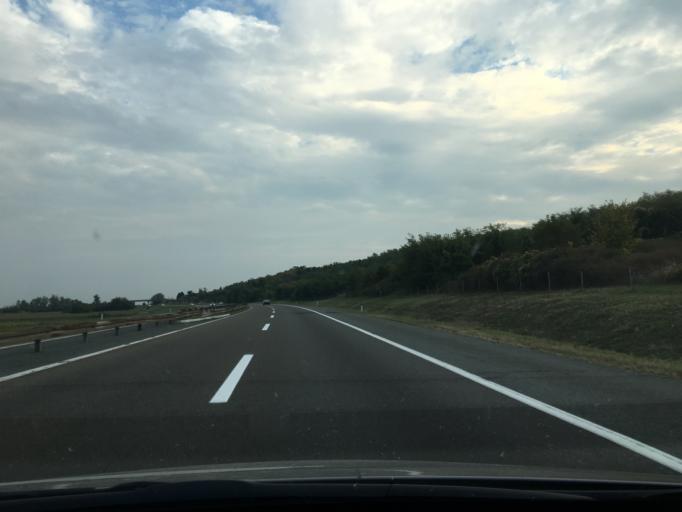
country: RS
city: Lugavcina
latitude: 44.4503
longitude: 21.0454
